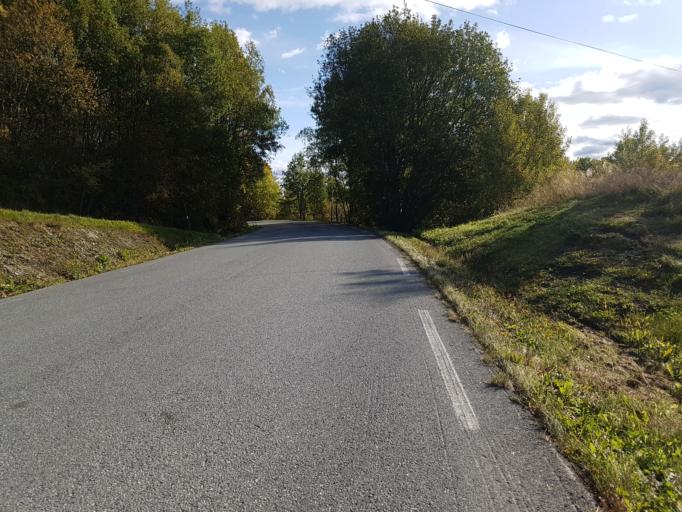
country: NO
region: Sor-Trondelag
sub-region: Malvik
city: Malvik
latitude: 63.3843
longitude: 10.5862
